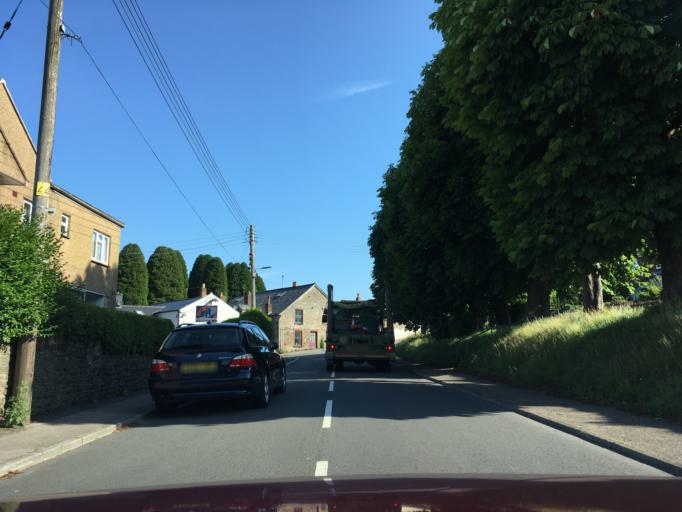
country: GB
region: England
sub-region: Gloucestershire
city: Cinderford
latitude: 51.8114
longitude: -2.5041
